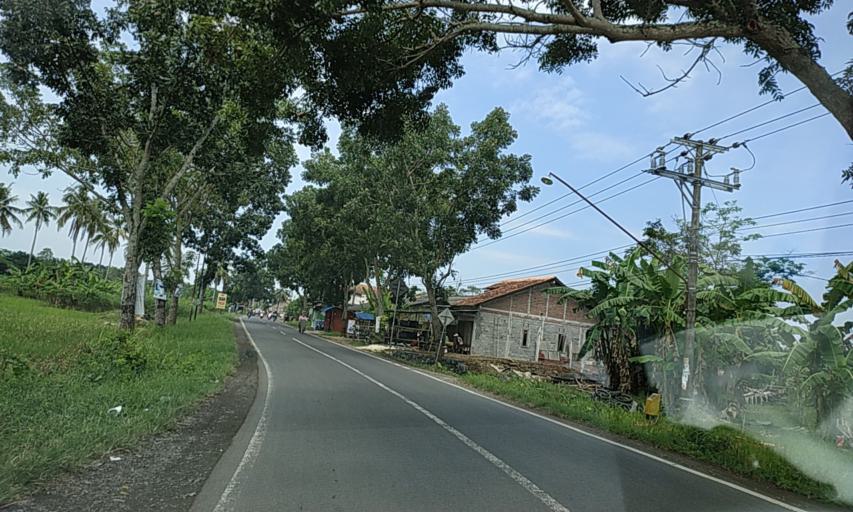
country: ID
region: Central Java
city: Sidareja
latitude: -7.4910
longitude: 108.7910
